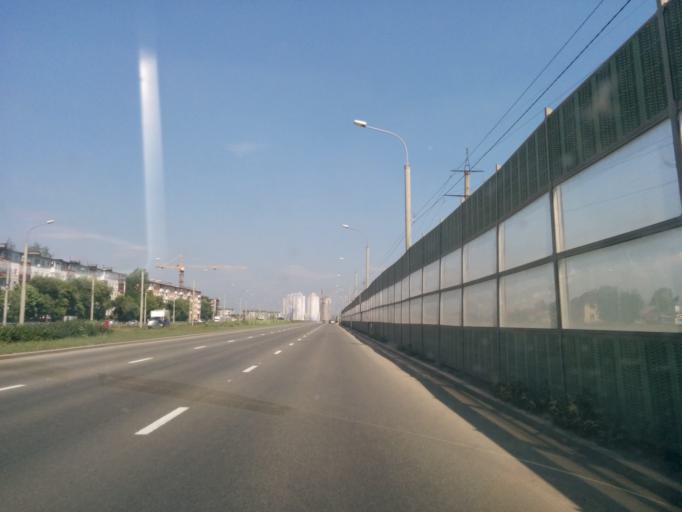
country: RU
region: Perm
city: Perm
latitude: 57.9925
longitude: 56.3015
